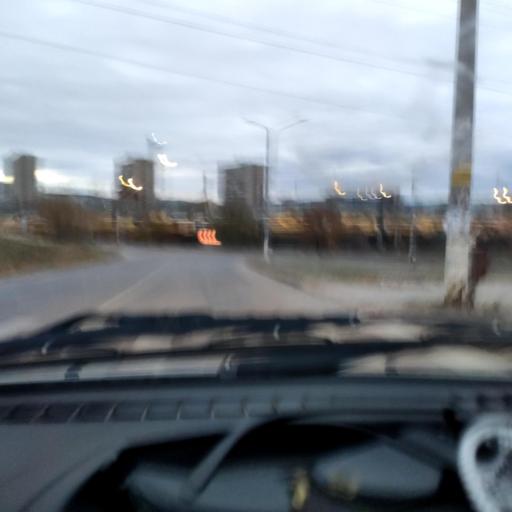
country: RU
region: Samara
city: Zhigulevsk
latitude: 53.4805
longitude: 49.5230
